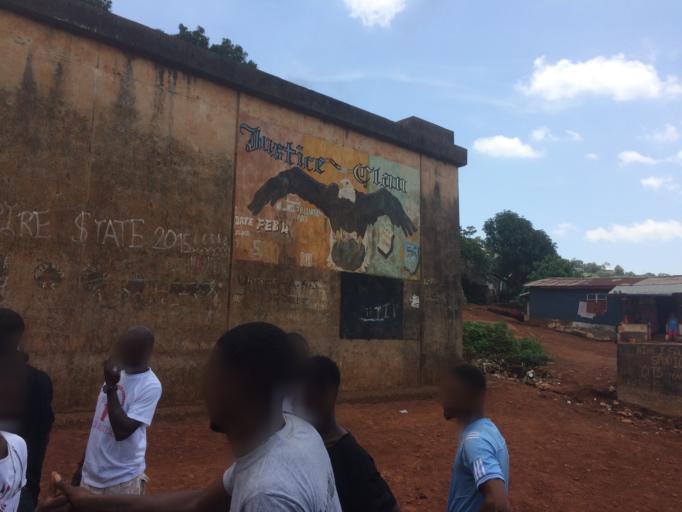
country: SL
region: Western Area
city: Freetown
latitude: 8.4690
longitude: -13.1979
